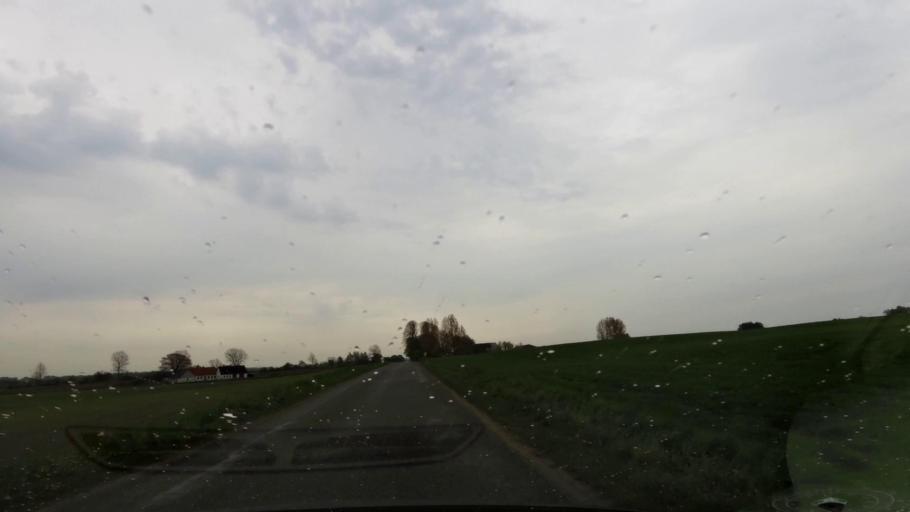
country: DK
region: South Denmark
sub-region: Svendborg Kommune
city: Svendborg
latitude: 55.1794
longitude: 10.5907
